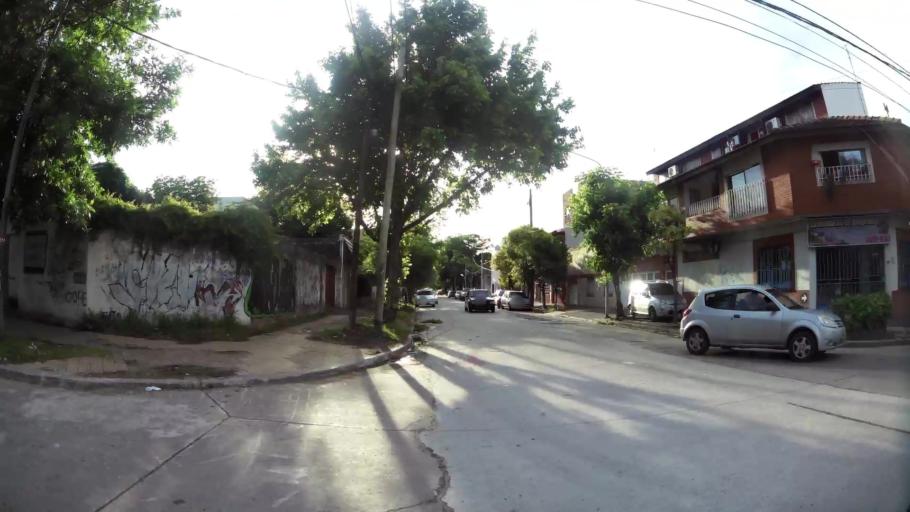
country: AR
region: Buenos Aires
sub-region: Partido de Moron
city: Moron
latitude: -34.6594
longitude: -58.6215
